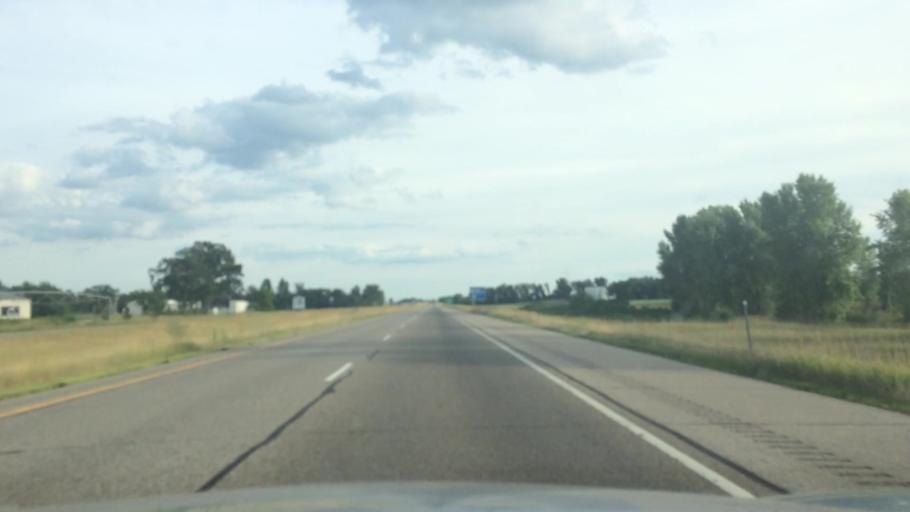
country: US
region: Wisconsin
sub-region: Portage County
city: Plover
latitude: 44.2261
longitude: -89.5246
